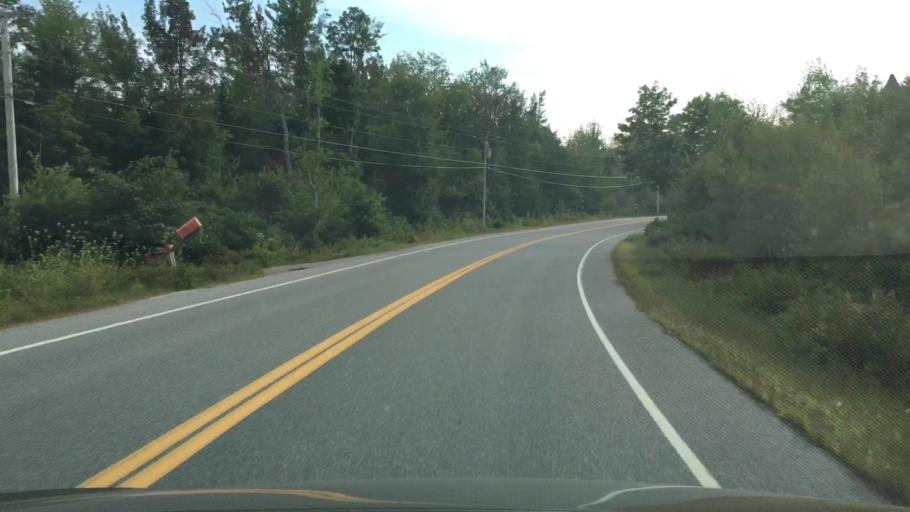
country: US
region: Maine
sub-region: Hancock County
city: Castine
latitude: 44.4345
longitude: -68.7950
